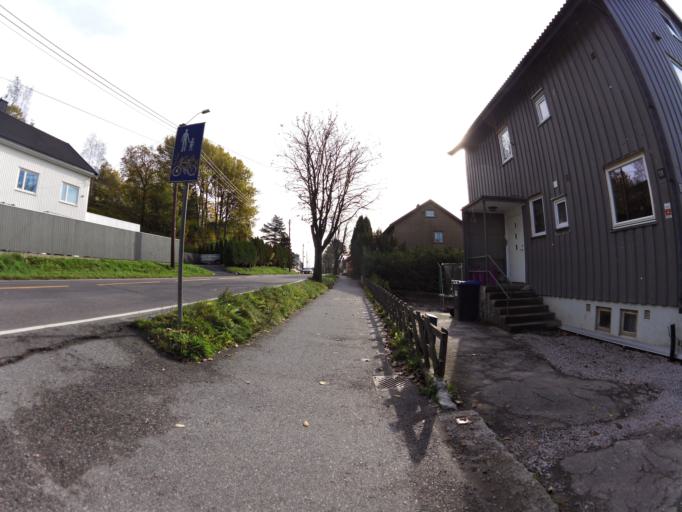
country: NO
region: Ostfold
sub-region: Fredrikstad
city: Fredrikstad
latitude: 59.2275
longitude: 10.9286
